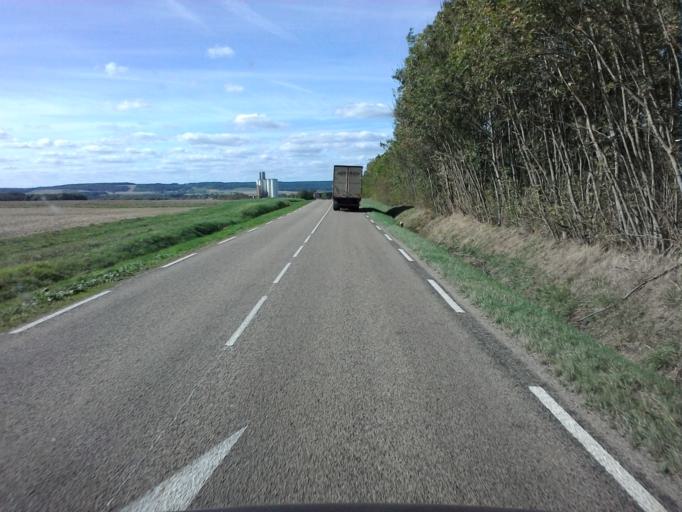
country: FR
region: Bourgogne
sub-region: Departement de la Cote-d'Or
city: Chatillon-sur-Seine
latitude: 47.9053
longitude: 4.6919
